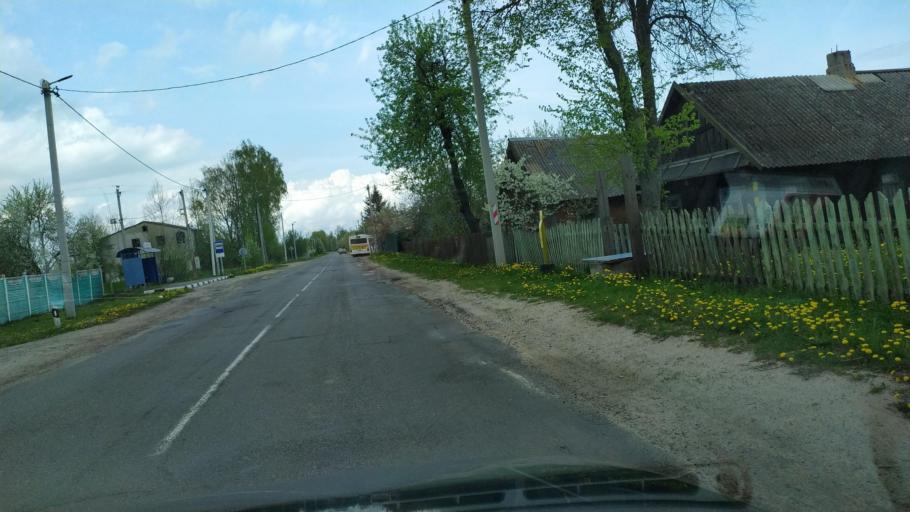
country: BY
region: Brest
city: Pruzhany
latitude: 52.5839
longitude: 24.4115
